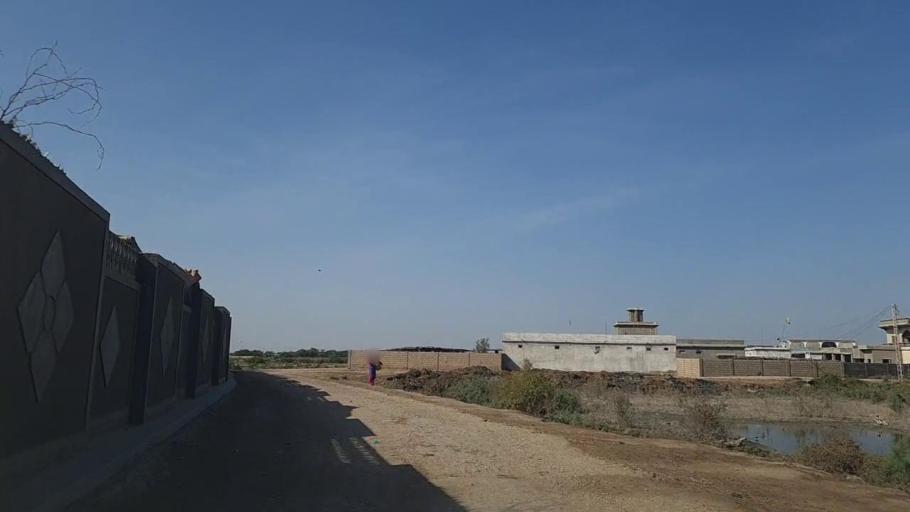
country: PK
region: Sindh
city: Thatta
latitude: 24.5933
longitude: 67.8848
